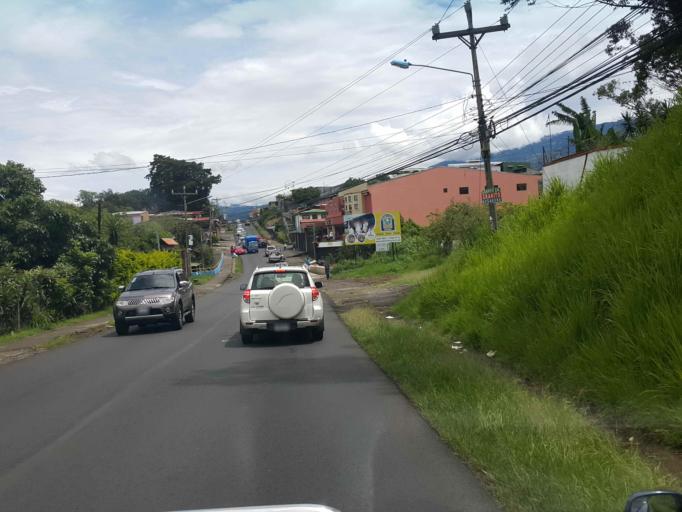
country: CR
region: Heredia
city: Heredia
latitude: 10.0077
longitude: -84.1176
